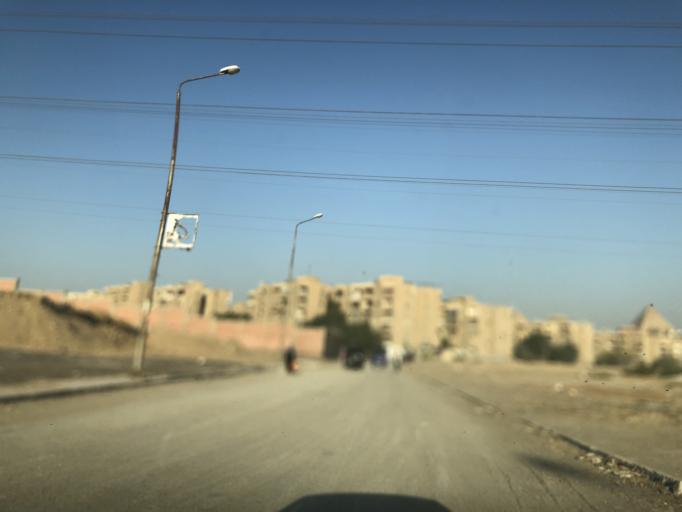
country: EG
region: Al Jizah
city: Al Jizah
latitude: 29.9842
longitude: 31.1099
